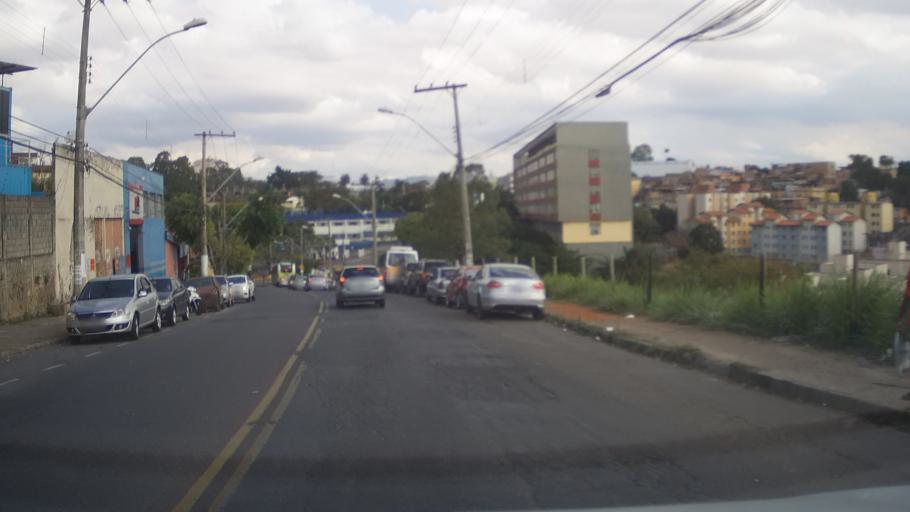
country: BR
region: Minas Gerais
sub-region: Belo Horizonte
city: Belo Horizonte
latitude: -19.8683
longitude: -43.9504
